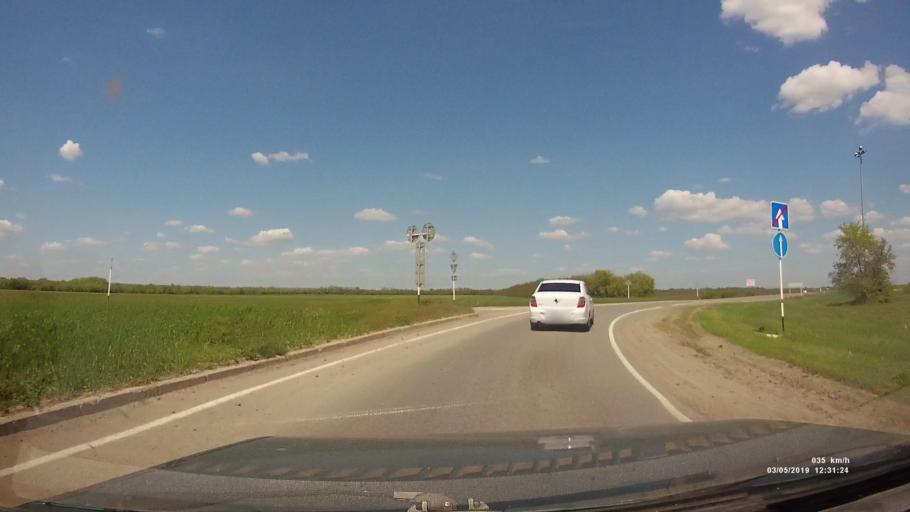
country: RU
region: Rostov
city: Semikarakorsk
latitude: 47.5045
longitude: 40.7491
